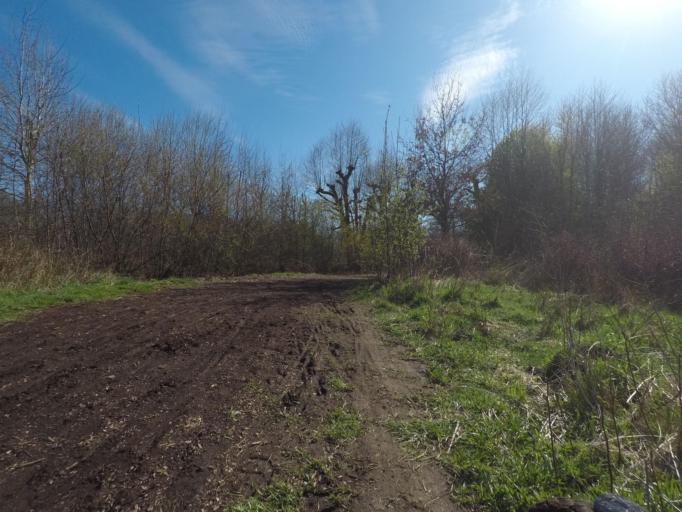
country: DE
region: Hamburg
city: Langenhorn
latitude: 53.6496
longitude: 9.9755
